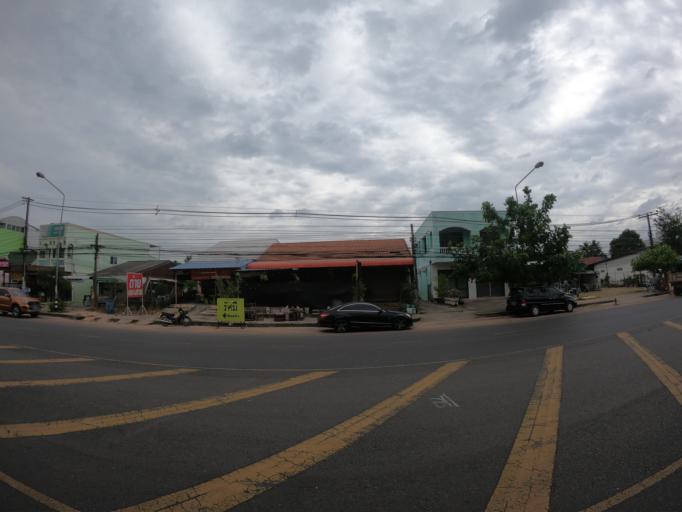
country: TH
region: Roi Et
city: Roi Et
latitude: 16.0636
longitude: 103.6663
